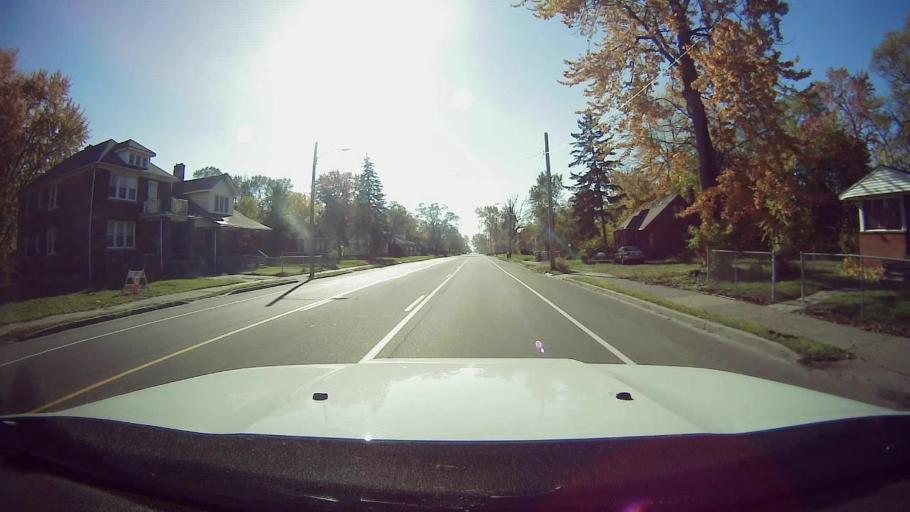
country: US
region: Michigan
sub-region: Wayne County
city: Dearborn
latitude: 42.3831
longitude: -83.1589
